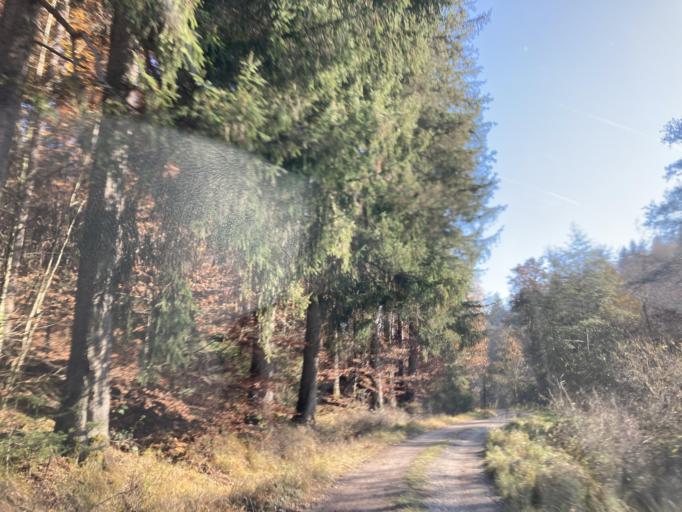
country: DE
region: Baden-Wuerttemberg
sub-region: Regierungsbezirk Stuttgart
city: Weil im Schonbuch
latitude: 48.5789
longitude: 9.0248
